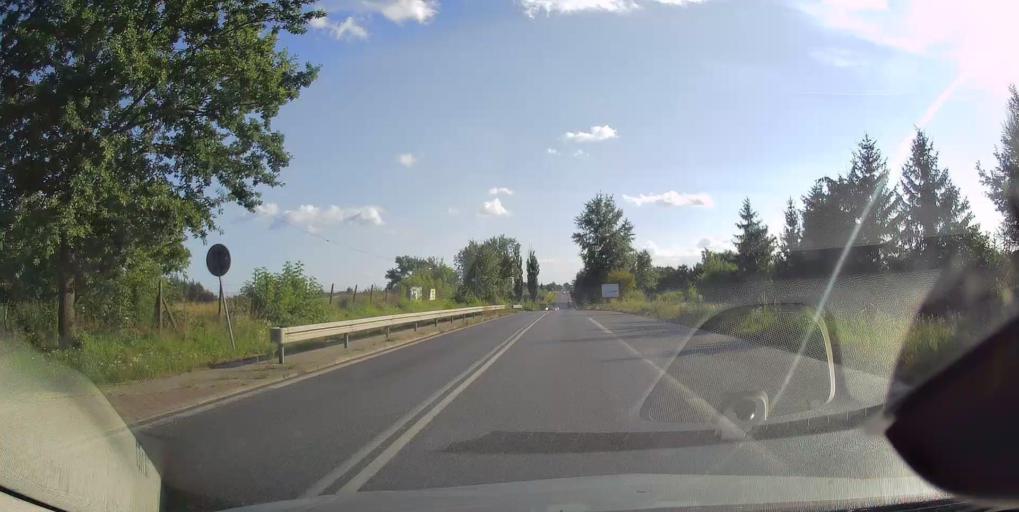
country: PL
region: Masovian Voivodeship
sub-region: Powiat grojecki
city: Grojec
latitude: 51.8580
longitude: 20.8511
